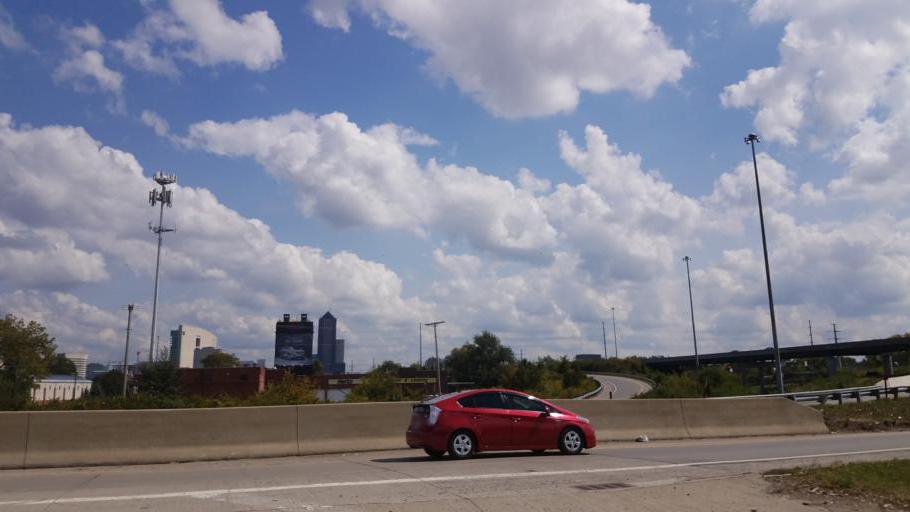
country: US
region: Ohio
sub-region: Franklin County
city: Columbus
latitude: 39.9522
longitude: -83.0177
